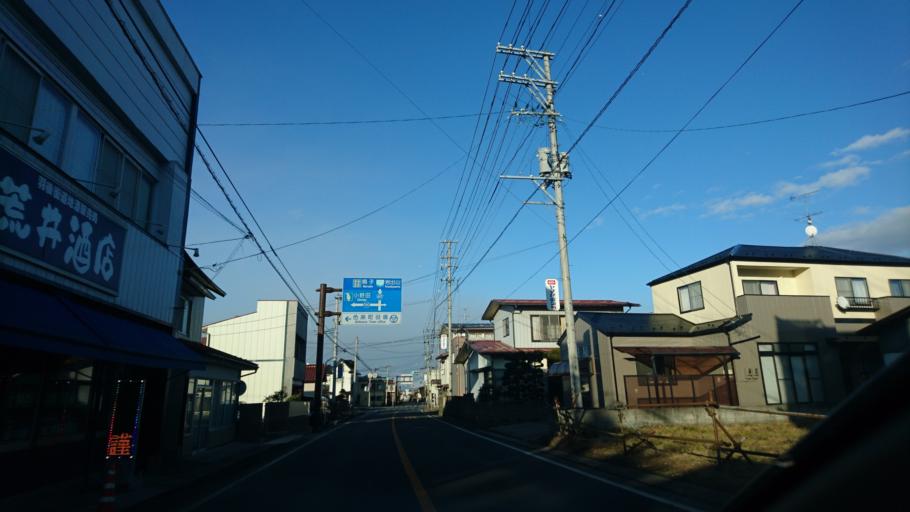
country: JP
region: Miyagi
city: Furukawa
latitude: 38.5467
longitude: 140.8512
